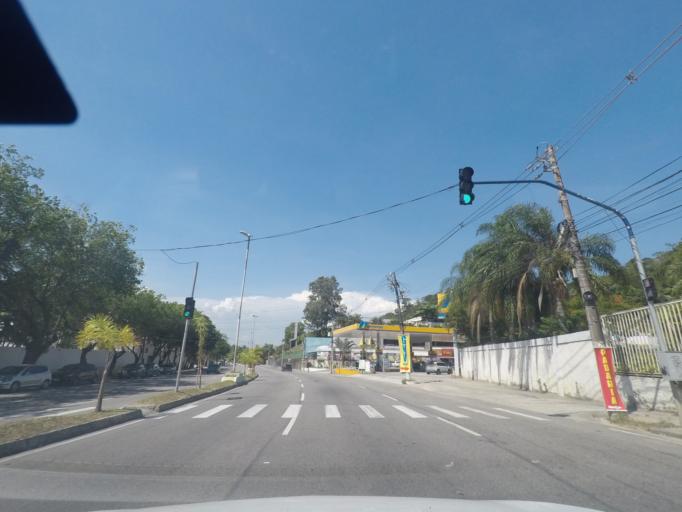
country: BR
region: Rio de Janeiro
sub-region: Niteroi
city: Niteroi
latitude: -22.9165
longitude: -43.0489
